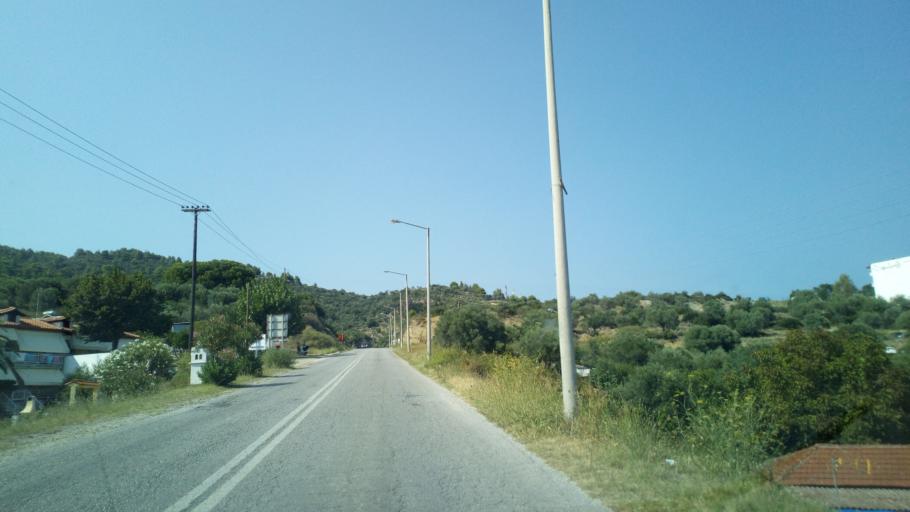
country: GR
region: Central Macedonia
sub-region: Nomos Chalkidikis
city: Sarti
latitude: 40.0976
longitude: 23.9761
